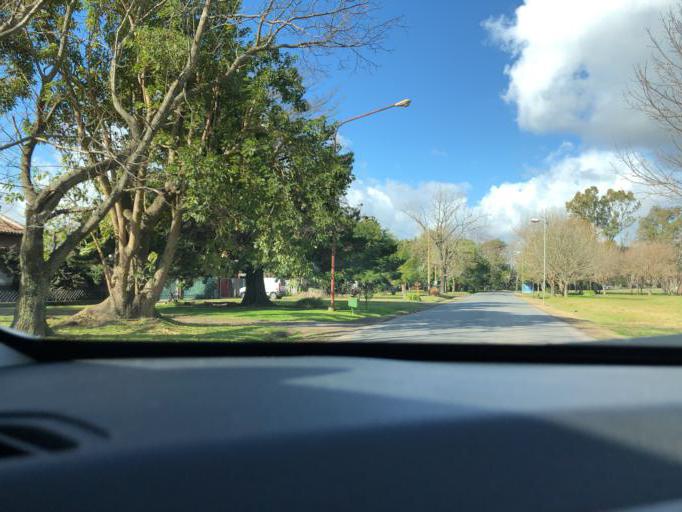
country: AR
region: Buenos Aires
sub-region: Partido de La Plata
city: La Plata
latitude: -34.8655
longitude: -58.0402
